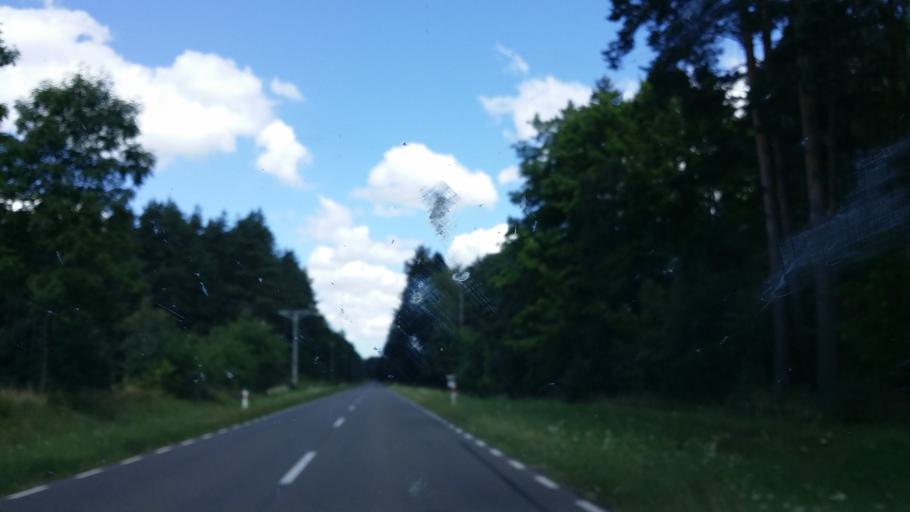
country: PL
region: West Pomeranian Voivodeship
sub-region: Powiat swidwinski
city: Slawoborze
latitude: 53.8639
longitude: 15.7307
